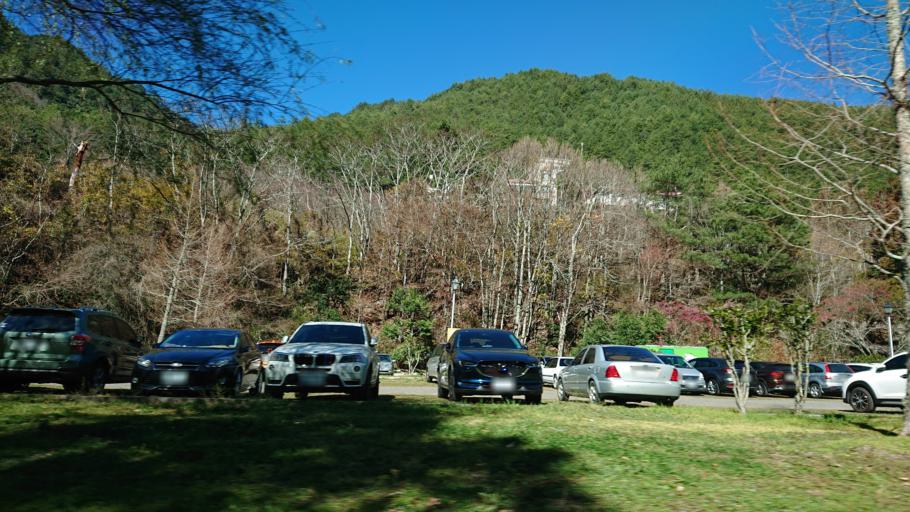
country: TW
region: Taiwan
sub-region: Hualien
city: Hualian
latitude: 24.3514
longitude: 121.3094
